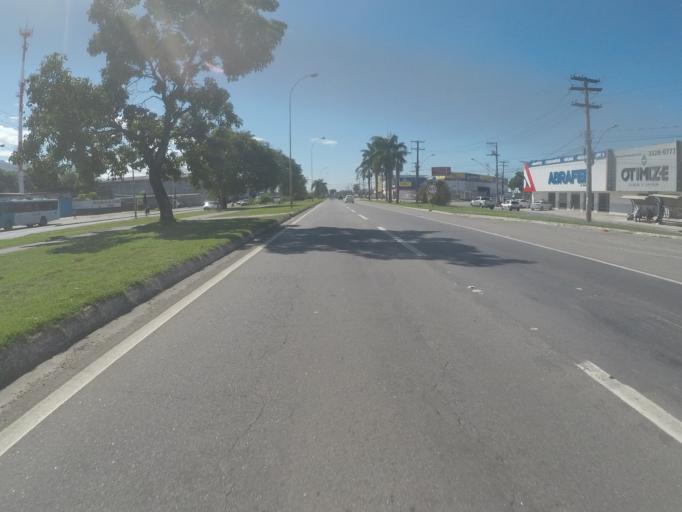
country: BR
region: Espirito Santo
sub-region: Serra
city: Serra
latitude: -20.2170
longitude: -40.2699
